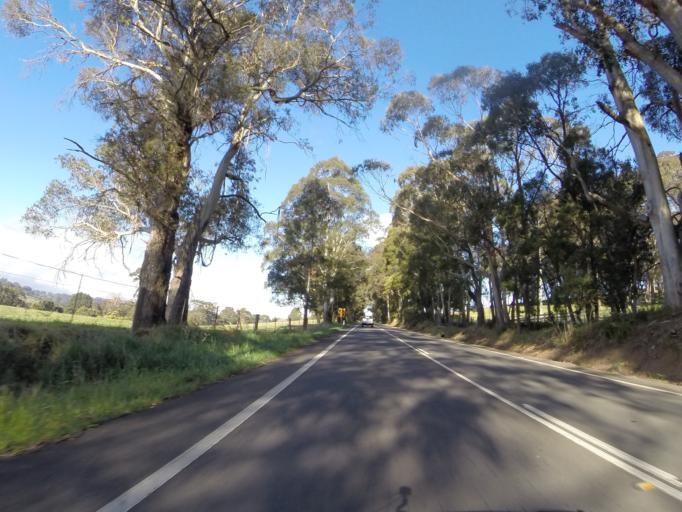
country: AU
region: New South Wales
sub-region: Wingecarribee
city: Bowral
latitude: -34.5827
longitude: 150.5199
